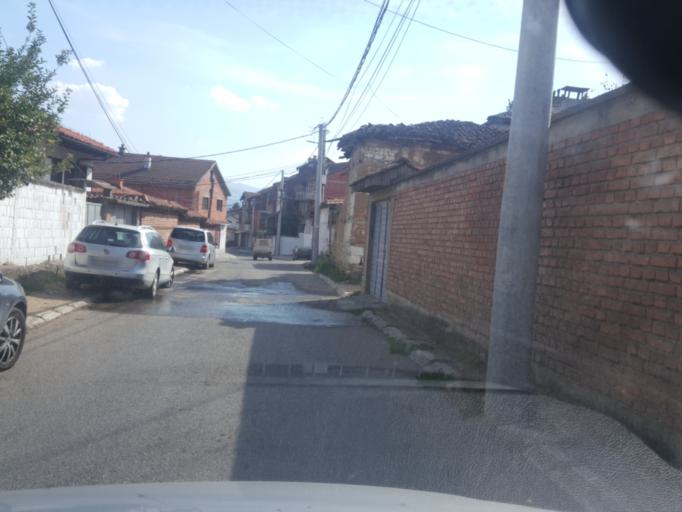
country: XK
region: Gjakova
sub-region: Komuna e Gjakoves
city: Gjakove
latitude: 42.3798
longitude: 20.4245
